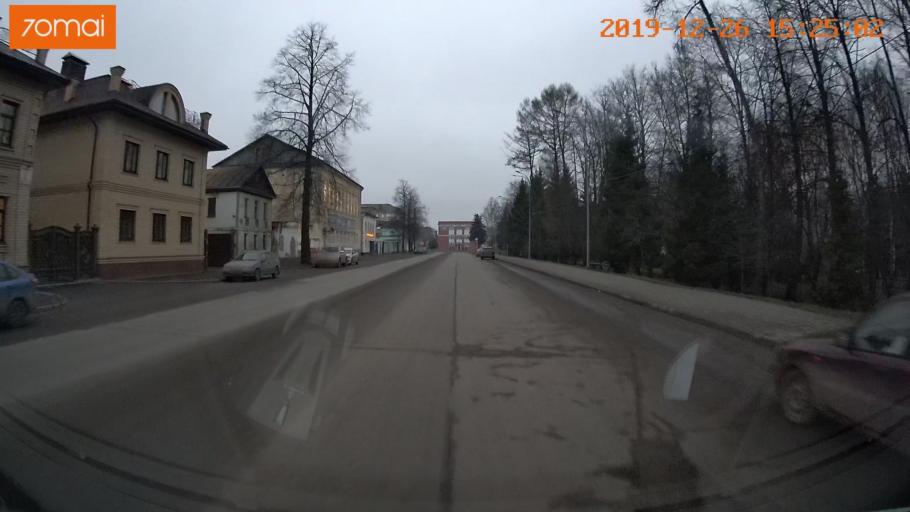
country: RU
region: Jaroslavl
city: Rybinsk
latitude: 58.0521
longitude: 38.8417
